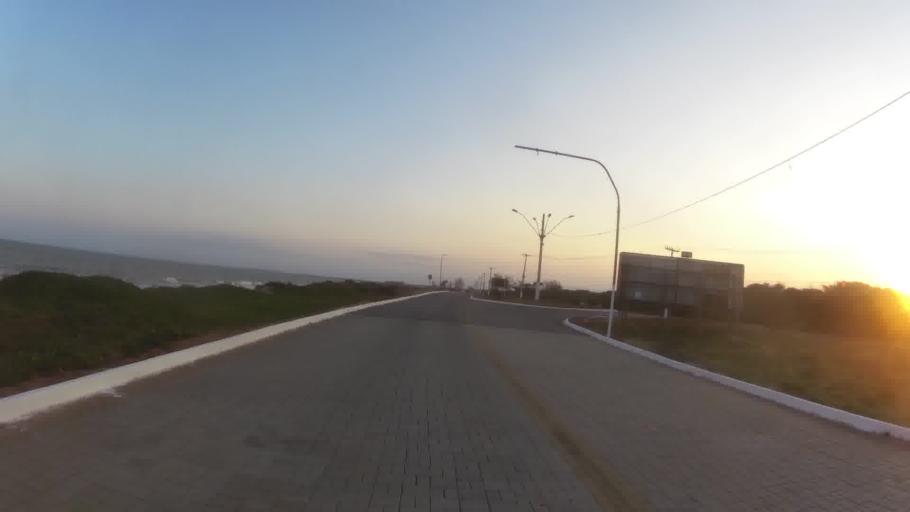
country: BR
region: Espirito Santo
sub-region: Piuma
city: Piuma
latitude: -20.9143
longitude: -40.7863
